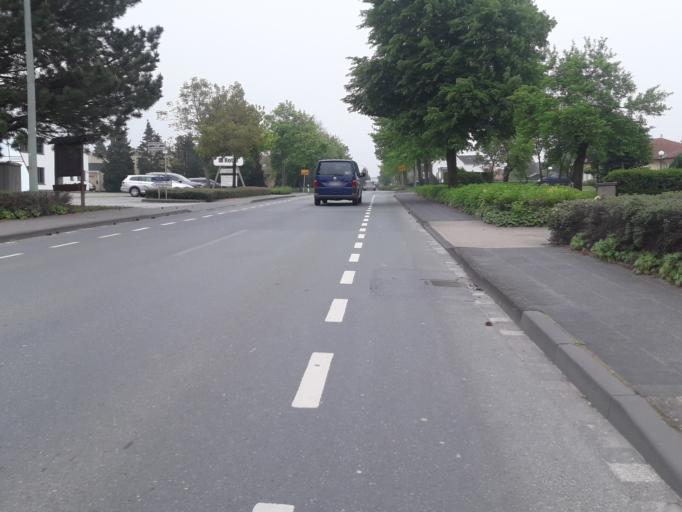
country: DE
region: North Rhine-Westphalia
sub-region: Regierungsbezirk Detmold
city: Salzkotten
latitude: 51.6396
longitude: 8.6679
